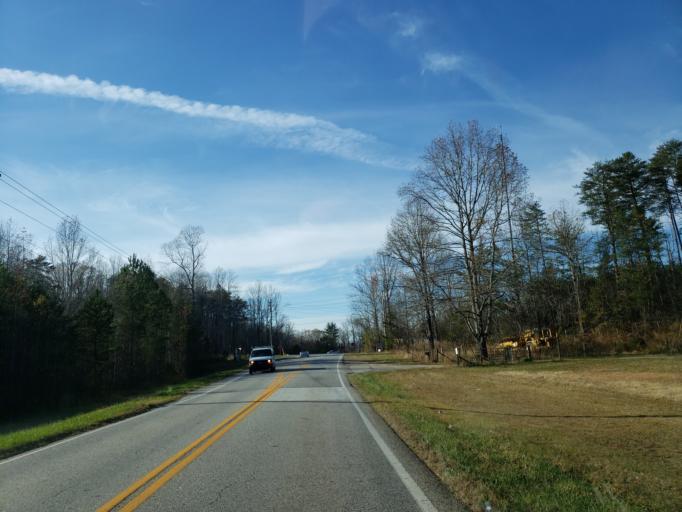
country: US
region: Georgia
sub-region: Lumpkin County
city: Dahlonega
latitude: 34.4654
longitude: -84.0195
